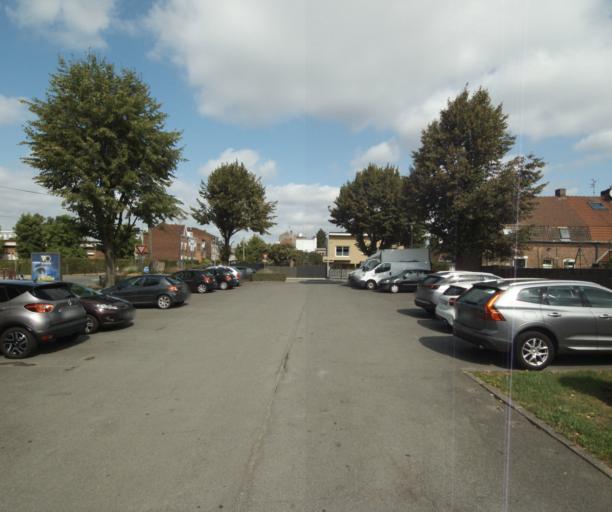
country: FR
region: Nord-Pas-de-Calais
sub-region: Departement du Nord
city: Lys-lez-Lannoy
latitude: 50.6707
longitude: 3.2141
